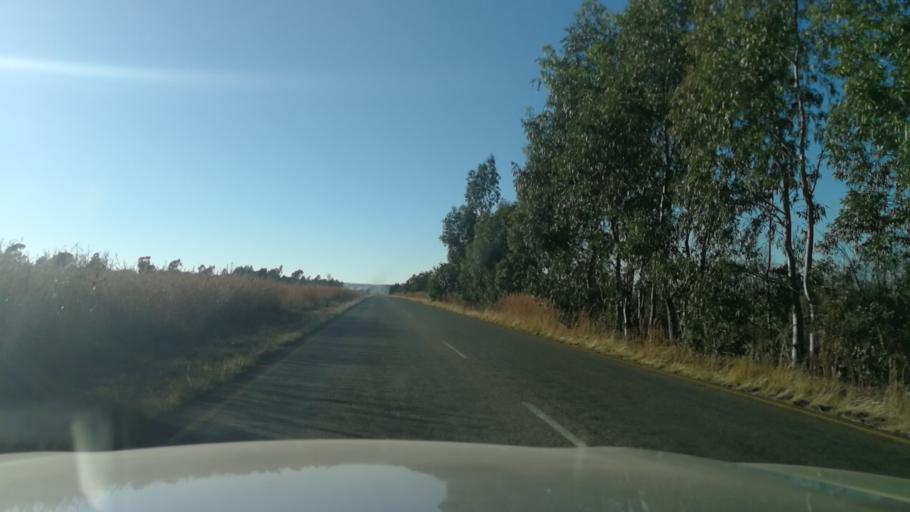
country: ZA
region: North-West
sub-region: Bojanala Platinum District Municipality
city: Koster
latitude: -25.9194
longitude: 27.0847
